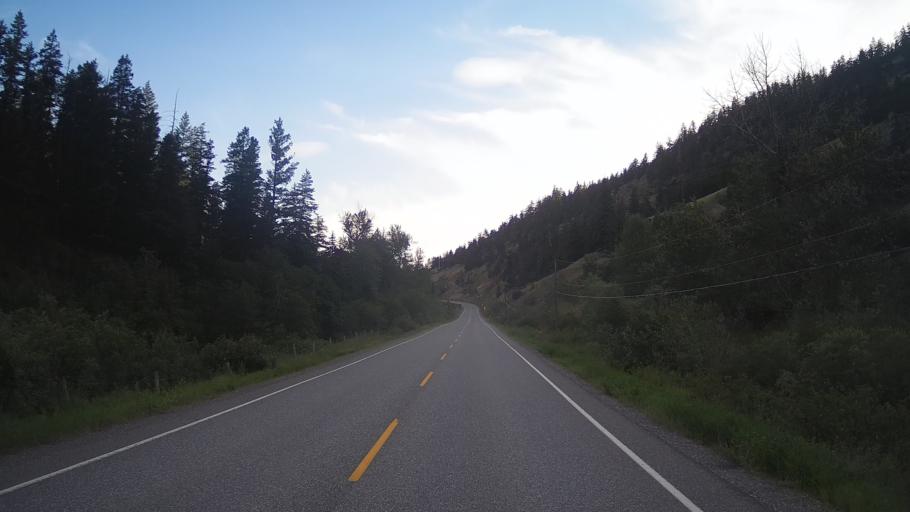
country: CA
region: British Columbia
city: Cache Creek
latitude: 50.8703
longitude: -121.5227
